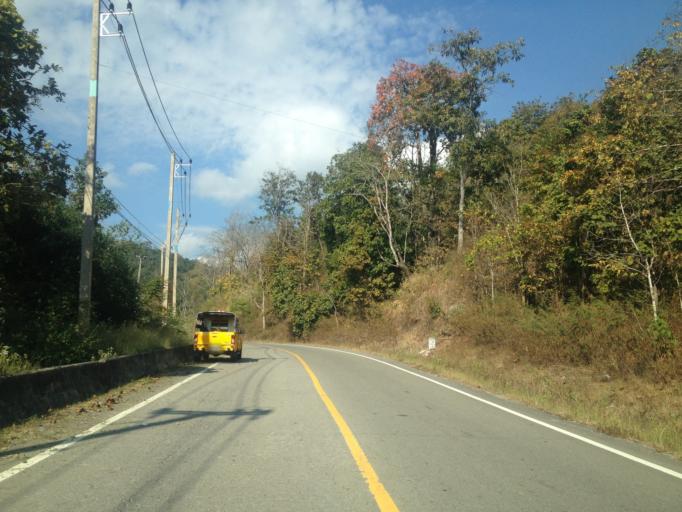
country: TH
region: Mae Hong Son
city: Ban Huai I Huak
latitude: 18.1342
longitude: 98.1799
